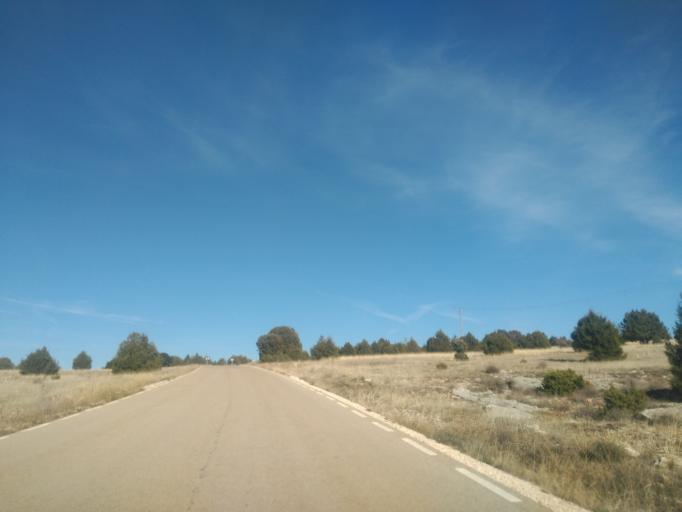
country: ES
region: Castille and Leon
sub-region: Provincia de Soria
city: Espejon
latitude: 41.8373
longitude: -3.2459
